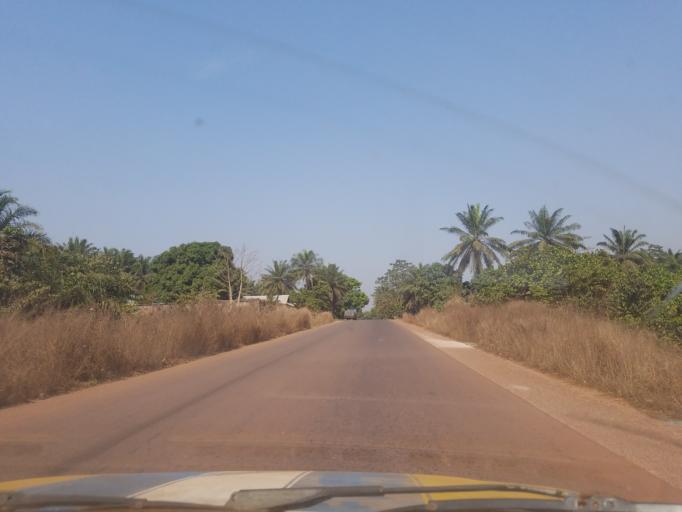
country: GN
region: Boke
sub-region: Boke Prefecture
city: Boke
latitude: 10.8300
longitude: -14.3677
